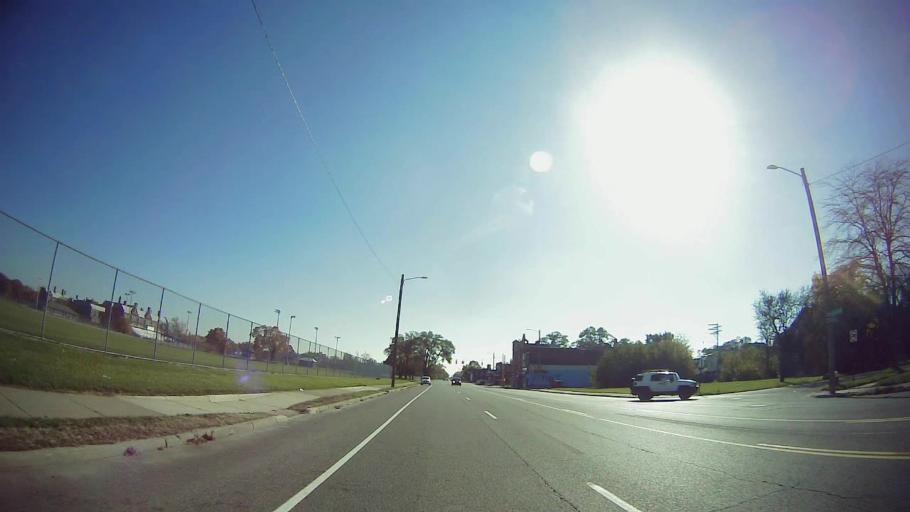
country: US
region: Michigan
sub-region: Wayne County
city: Highland Park
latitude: 42.3830
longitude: -83.1151
